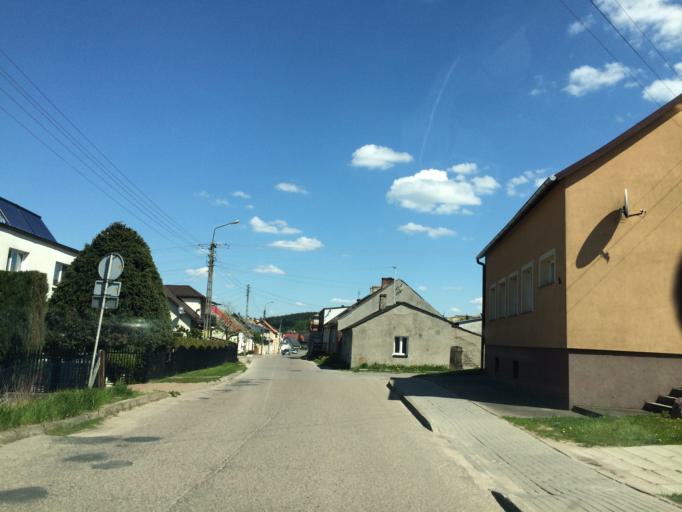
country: PL
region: Warmian-Masurian Voivodeship
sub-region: Powiat nowomiejski
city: Kurzetnik
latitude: 53.3975
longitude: 19.5735
